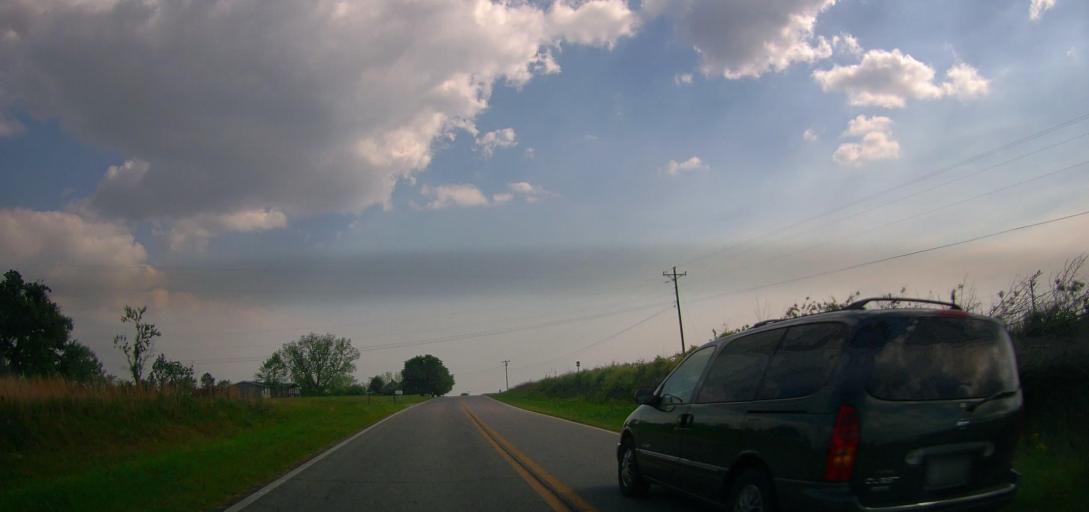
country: US
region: Georgia
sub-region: Laurens County
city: East Dublin
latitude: 32.6104
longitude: -82.8683
